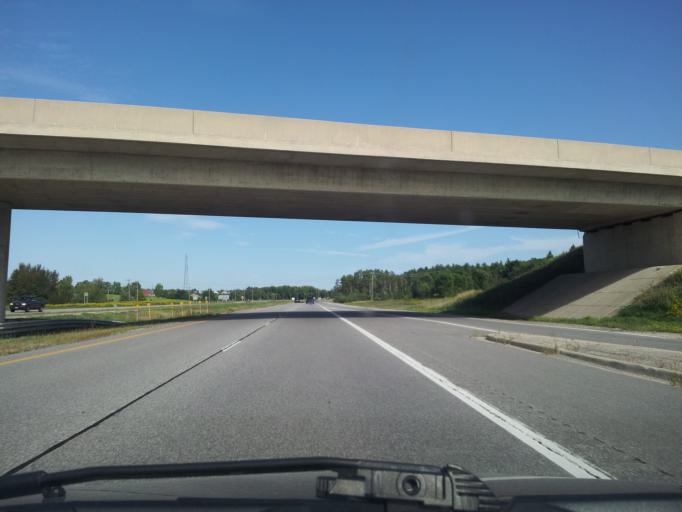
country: CA
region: Ontario
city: Kitchener
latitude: 43.4054
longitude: -80.5975
